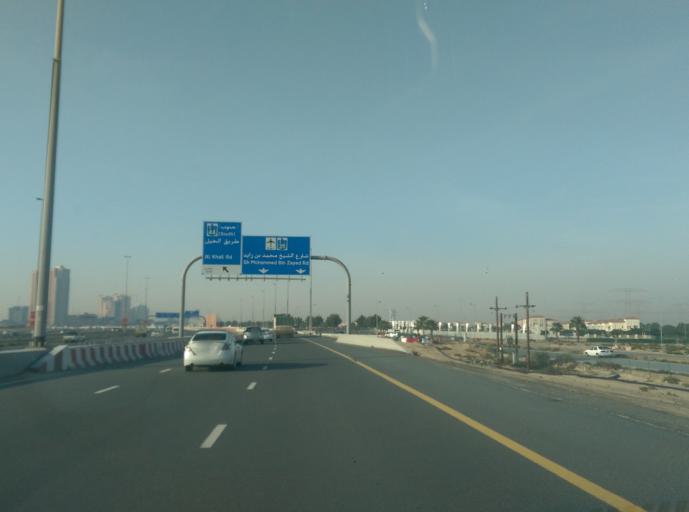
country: AE
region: Dubai
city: Dubai
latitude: 25.0602
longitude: 55.1960
